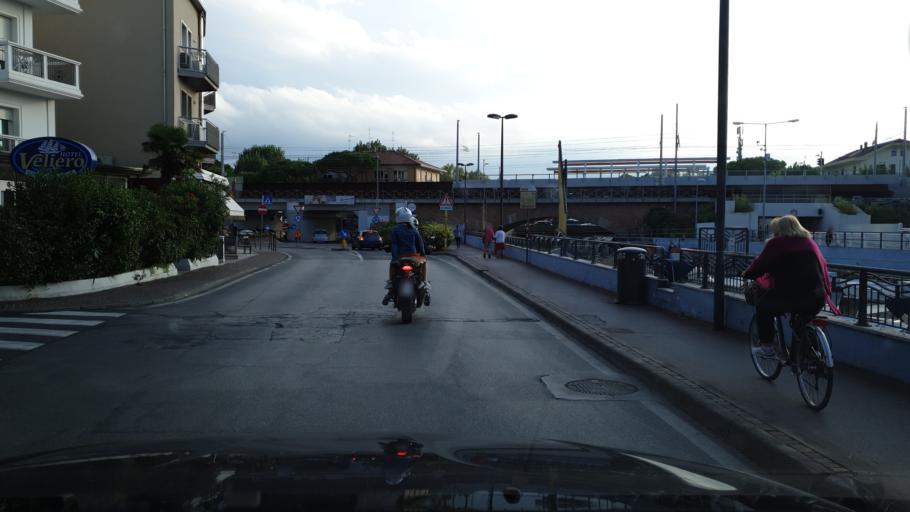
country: IT
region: Emilia-Romagna
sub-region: Provincia di Rimini
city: Riccione
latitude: 44.0040
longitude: 12.6544
